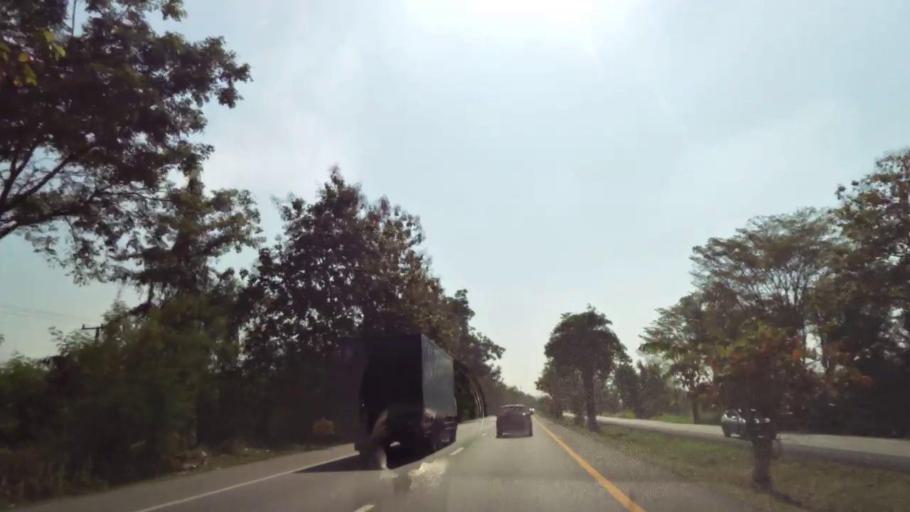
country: TH
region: Phichit
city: Bueng Na Rang
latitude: 16.0581
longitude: 100.1224
